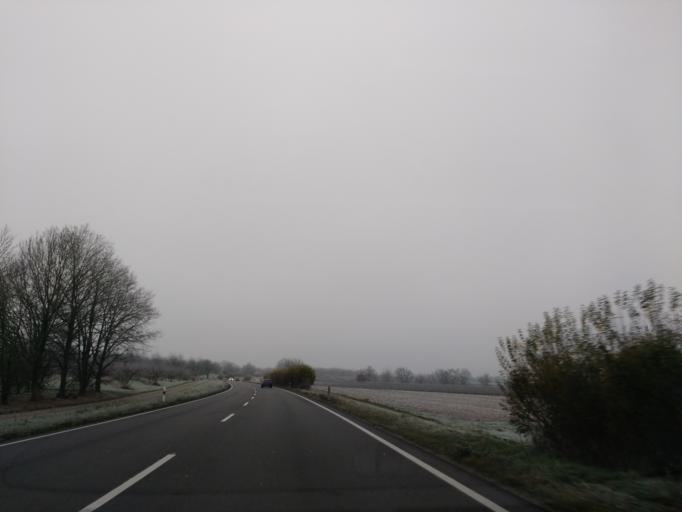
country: DE
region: Baden-Wuerttemberg
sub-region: Freiburg Region
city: Appenweier
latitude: 48.5385
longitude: 8.0161
